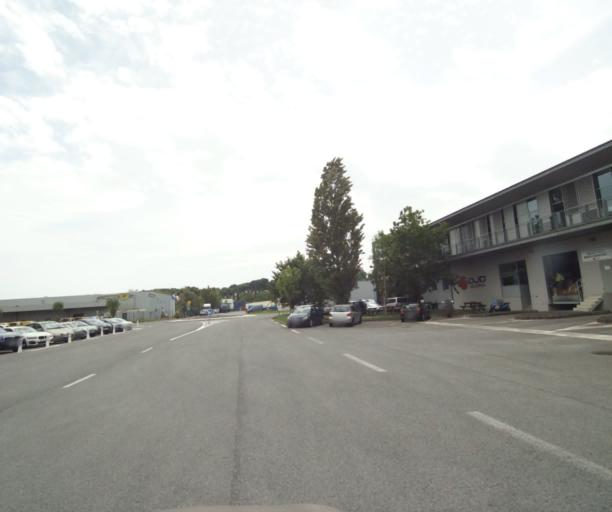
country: FR
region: Aquitaine
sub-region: Departement des Pyrenees-Atlantiques
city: Mouguerre
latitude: 43.4888
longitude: -1.4248
